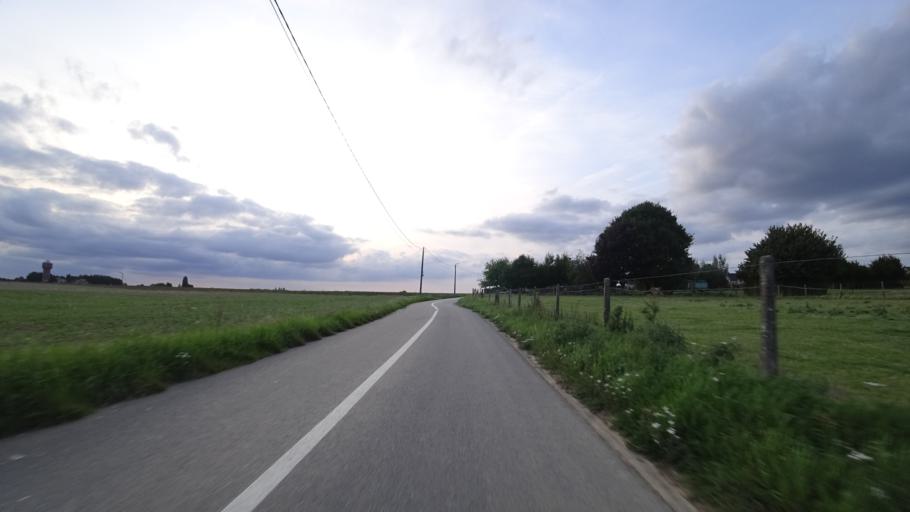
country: BE
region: Wallonia
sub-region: Province de Namur
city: Namur
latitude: 50.5194
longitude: 4.8677
